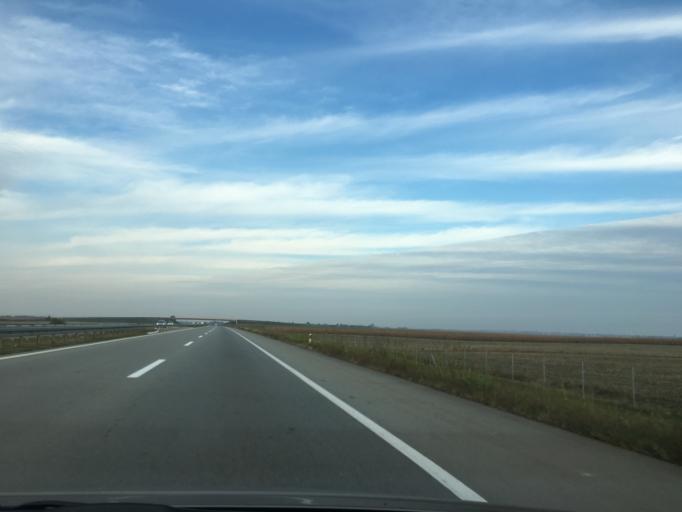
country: RS
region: Autonomna Pokrajina Vojvodina
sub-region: Juznobacki Okrug
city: Kovilj
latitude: 45.2564
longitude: 20.0051
